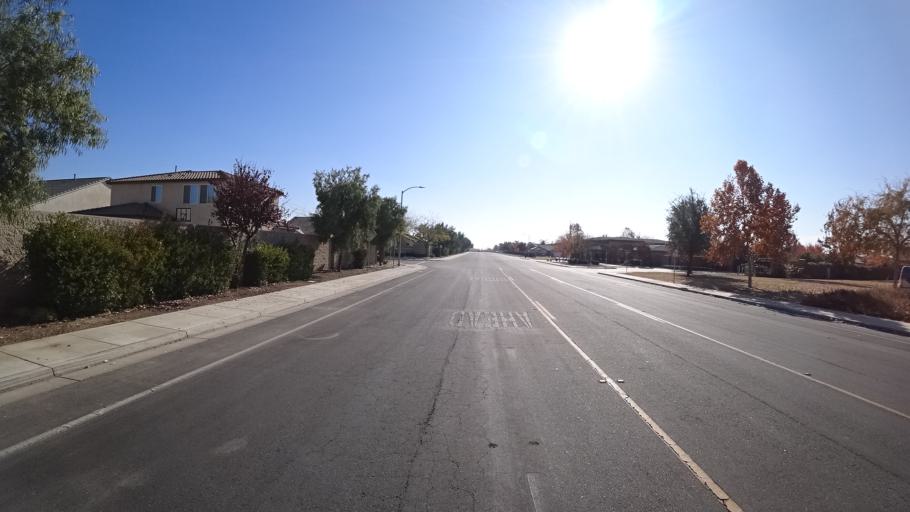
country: US
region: California
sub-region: Kern County
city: Greenacres
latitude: 35.3024
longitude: -119.1187
